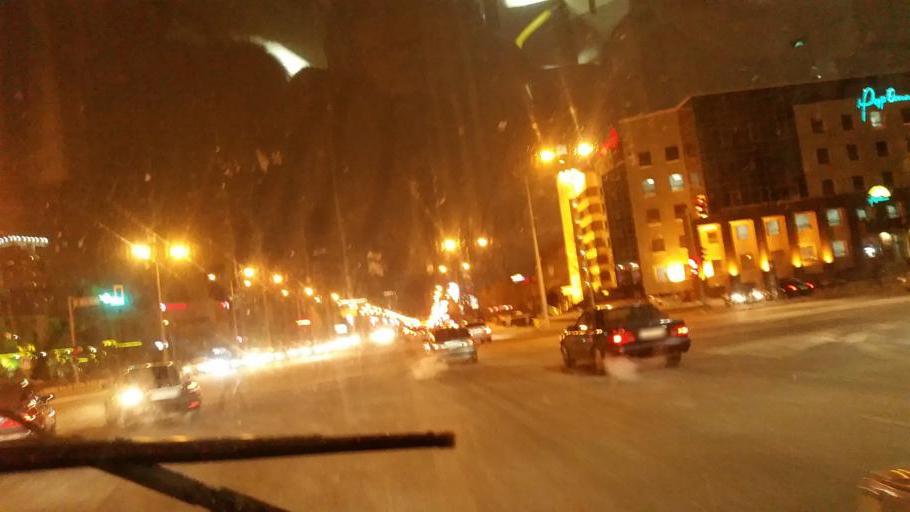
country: KZ
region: Astana Qalasy
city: Astana
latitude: 51.1515
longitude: 71.4561
